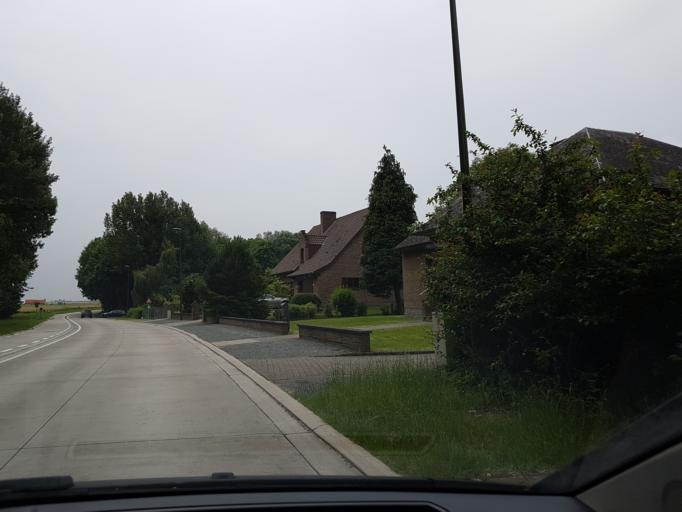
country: BE
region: Flanders
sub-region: Provincie Vlaams-Brabant
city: Steenokkerzeel
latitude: 50.9114
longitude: 4.5201
